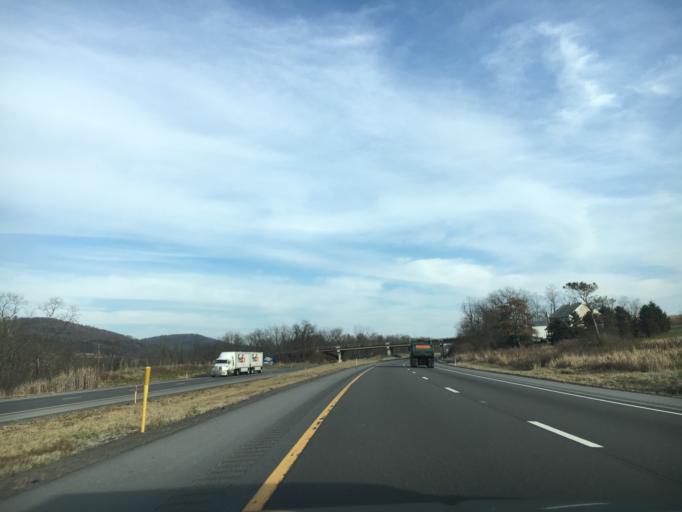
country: US
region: Pennsylvania
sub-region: Montour County
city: Mechanicsville
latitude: 41.0022
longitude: -76.5951
